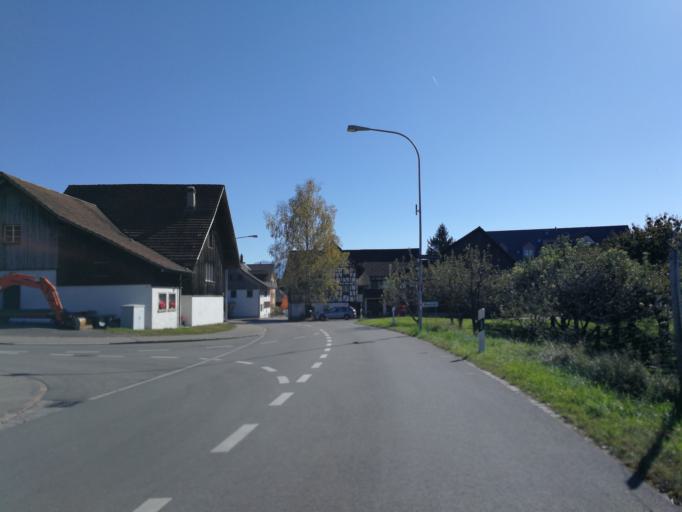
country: CH
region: Zurich
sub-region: Bezirk Hinwil
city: Wolfhausen
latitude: 47.2606
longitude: 8.7923
